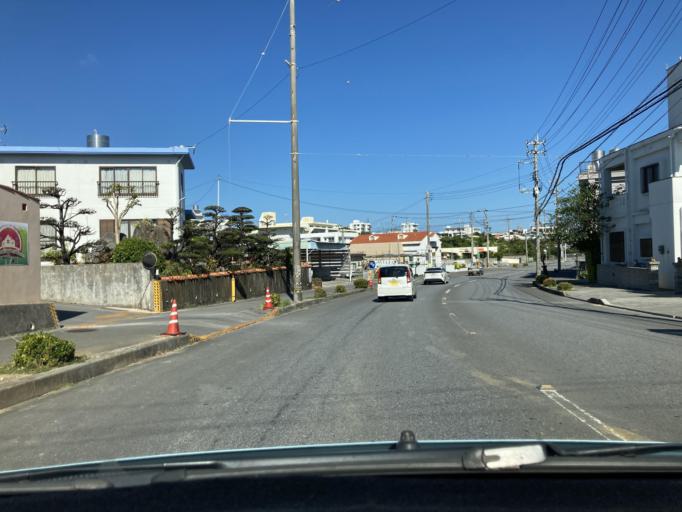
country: JP
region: Okinawa
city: Gushikawa
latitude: 26.3775
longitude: 127.8647
